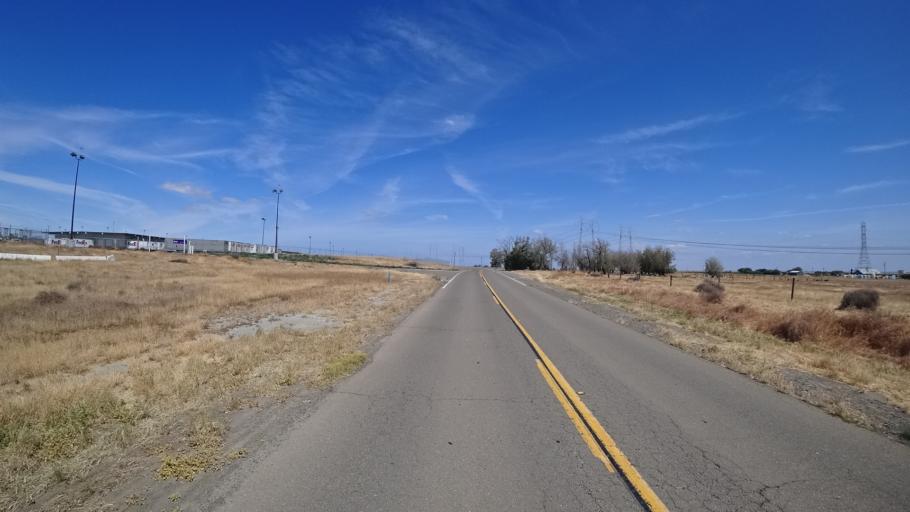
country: US
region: California
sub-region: Kings County
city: Kettleman City
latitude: 35.9892
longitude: -119.9536
